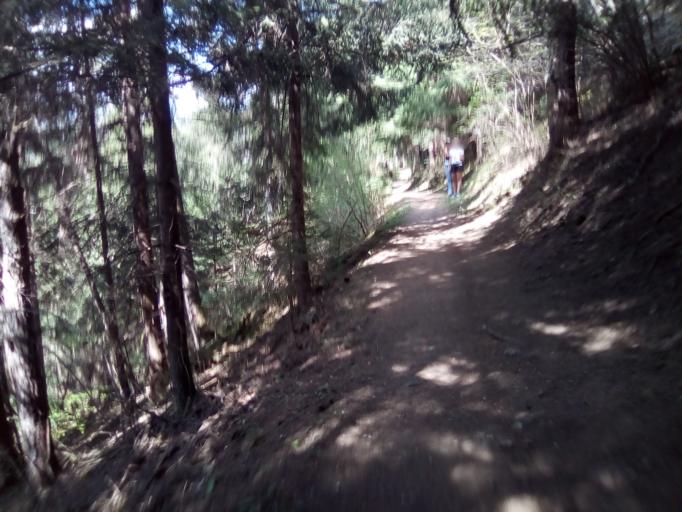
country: CH
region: Valais
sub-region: Entremont District
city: Orsieres
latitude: 46.0408
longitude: 7.1497
